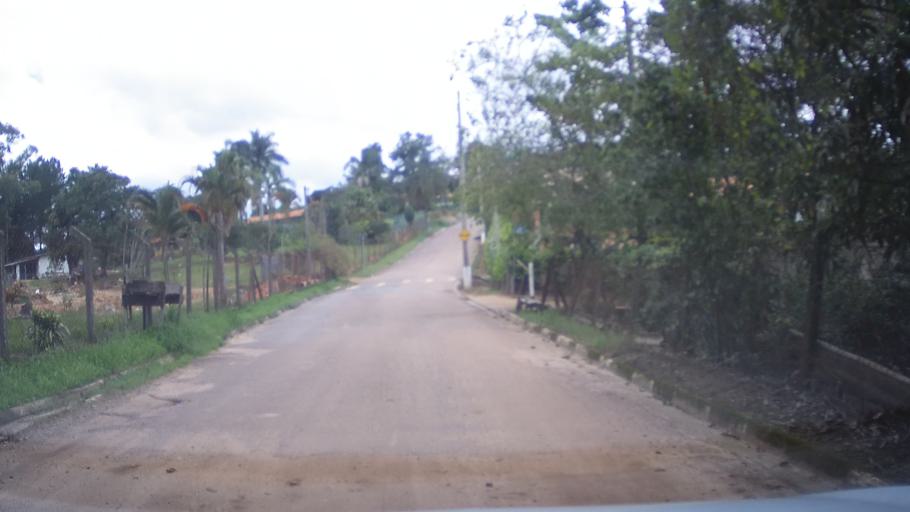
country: BR
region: Sao Paulo
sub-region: Vinhedo
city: Vinhedo
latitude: -23.0084
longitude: -46.9560
